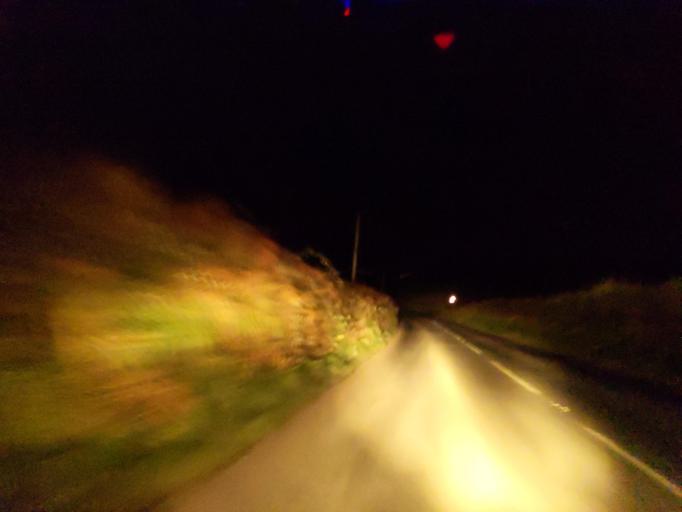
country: GB
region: England
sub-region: Cornwall
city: Saltash
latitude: 50.3540
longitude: -4.2600
